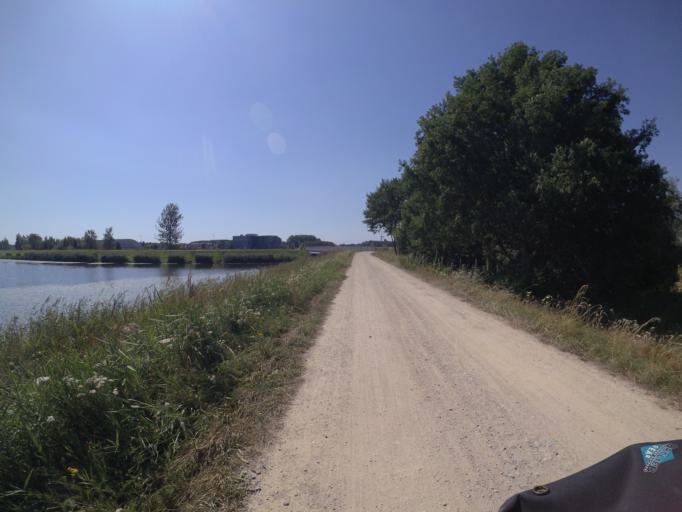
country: NL
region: North Brabant
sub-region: Gemeente 's-Hertogenbosch
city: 's-Hertogenbosch
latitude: 51.6944
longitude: 5.3539
